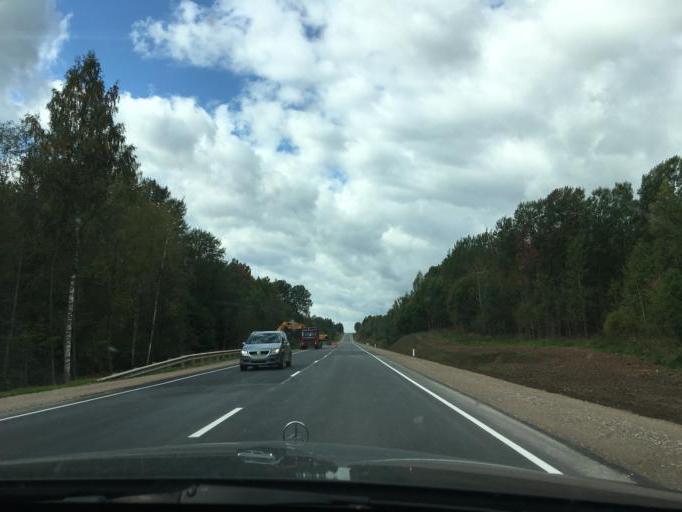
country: RU
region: Tverskaya
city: Toropets
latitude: 56.3102
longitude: 31.1407
